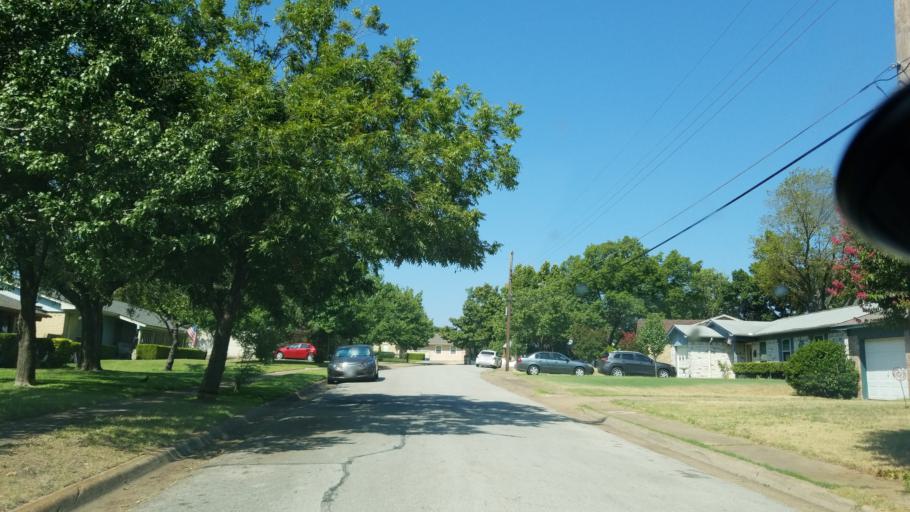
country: US
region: Texas
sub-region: Dallas County
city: Duncanville
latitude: 32.6586
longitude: -96.9044
